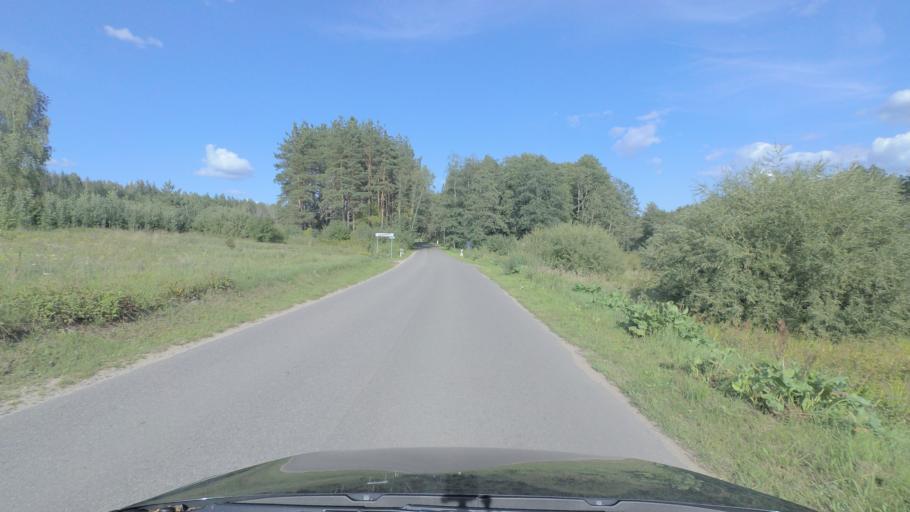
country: LT
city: Nemencine
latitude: 54.8613
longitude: 25.3944
